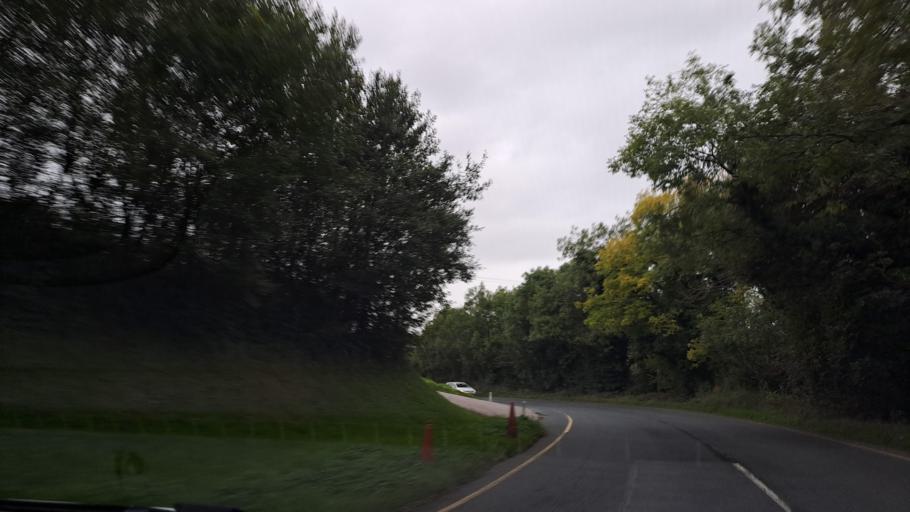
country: IE
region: Ulster
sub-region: County Monaghan
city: Monaghan
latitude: 54.2316
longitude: -6.9589
